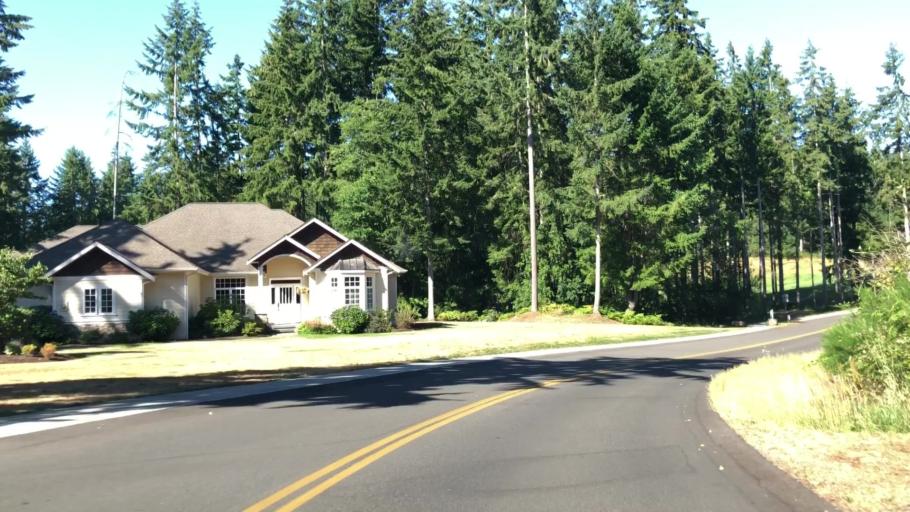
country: US
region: Washington
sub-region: Kitsap County
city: Indianola
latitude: 47.7692
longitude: -122.5258
